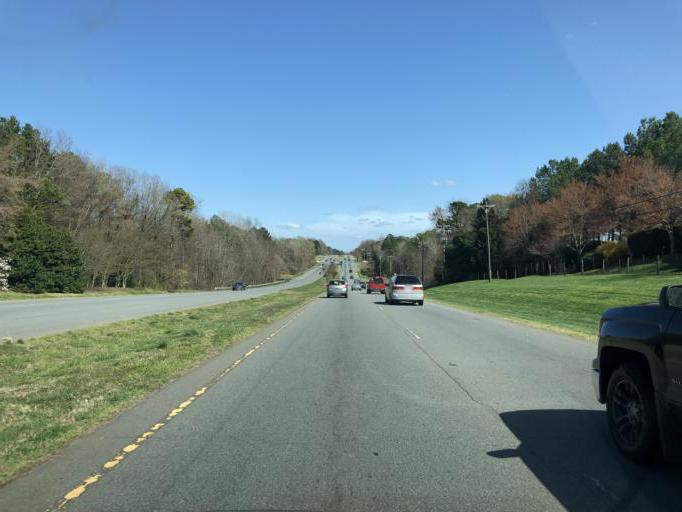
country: US
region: North Carolina
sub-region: Mecklenburg County
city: Huntersville
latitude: 35.3324
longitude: -80.8050
